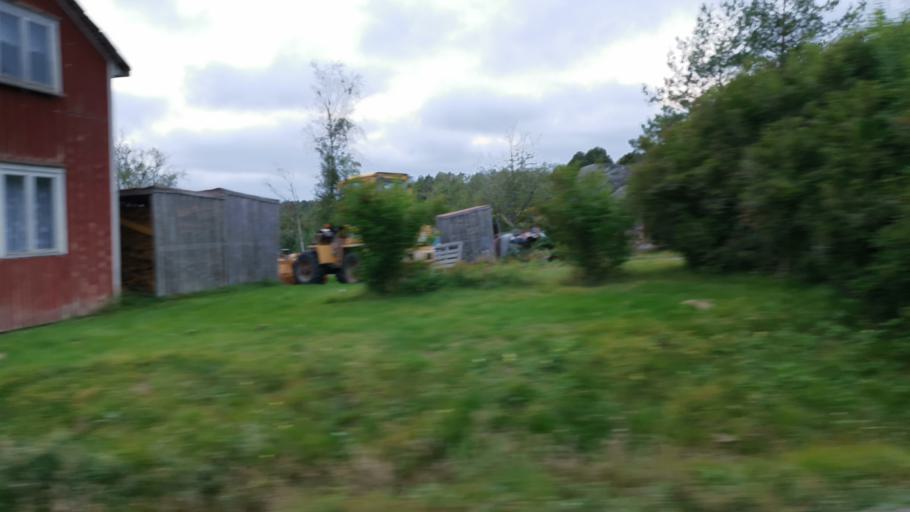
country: SE
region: Vaestra Goetaland
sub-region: Tanums Kommun
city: Tanumshede
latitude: 58.6412
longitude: 11.3400
